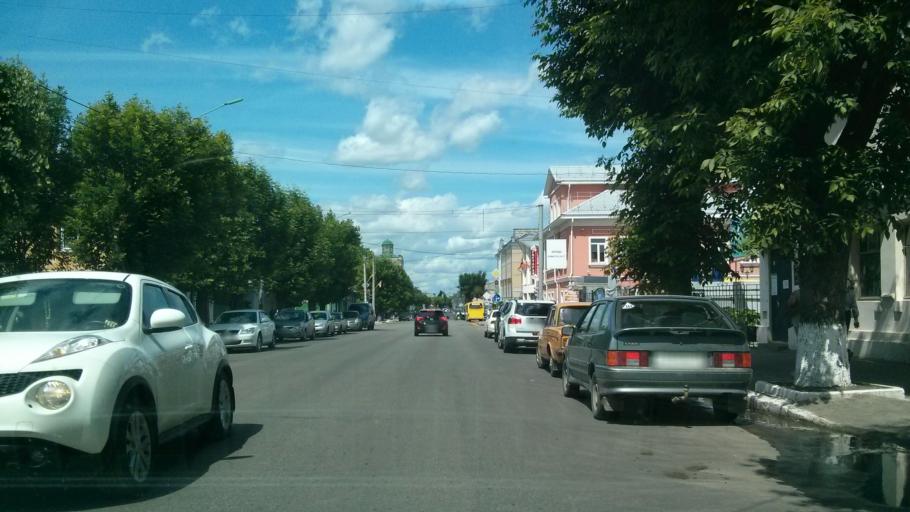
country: RU
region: Vladimir
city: Murom
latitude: 55.5759
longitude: 42.0548
